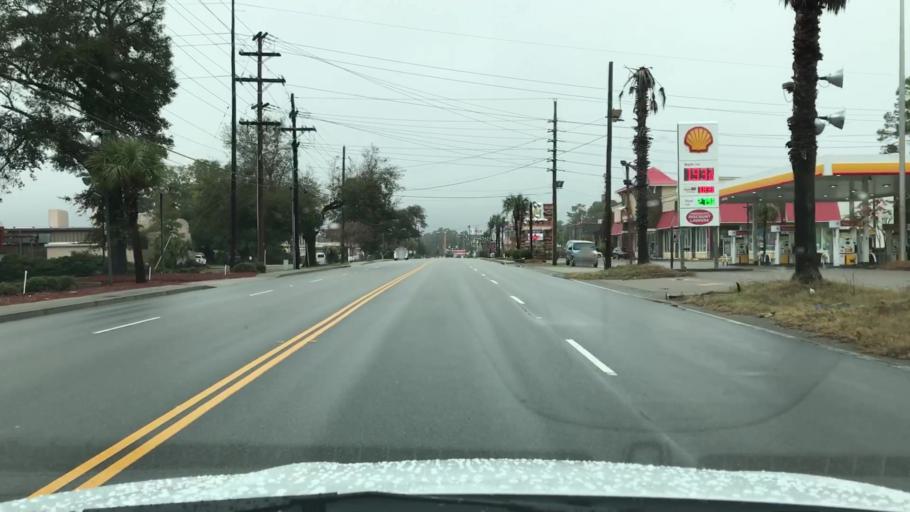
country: US
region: South Carolina
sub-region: Horry County
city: North Myrtle Beach
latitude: 33.7751
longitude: -78.7905
